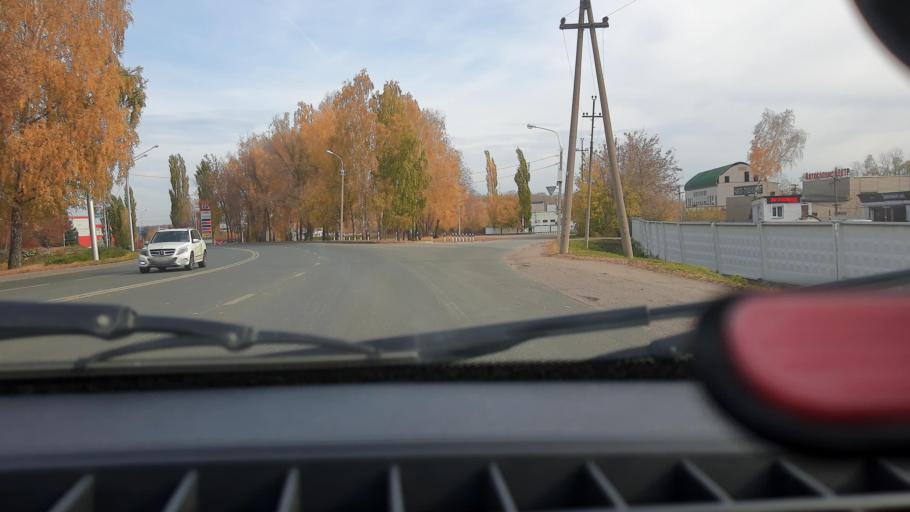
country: RU
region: Bashkortostan
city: Mikhaylovka
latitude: 54.7026
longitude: 55.8444
